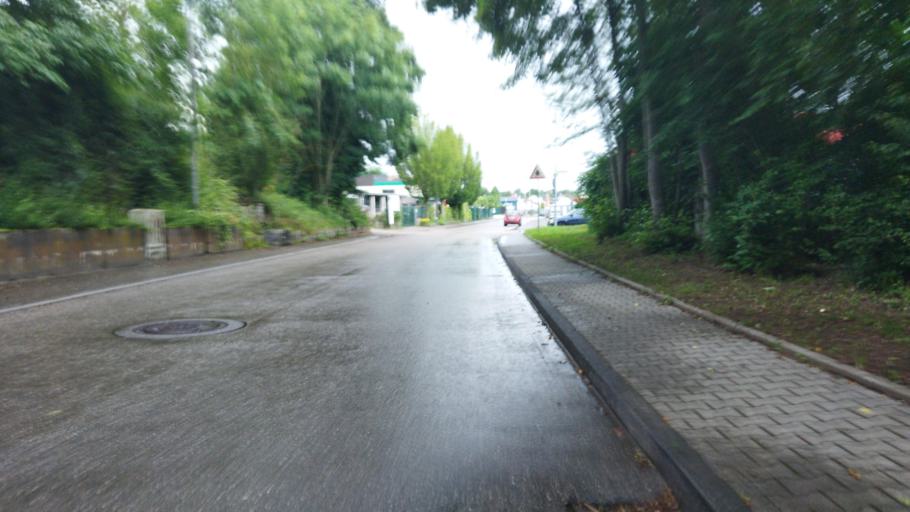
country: DE
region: Baden-Wuerttemberg
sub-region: Regierungsbezirk Stuttgart
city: Kirchardt
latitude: 49.2019
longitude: 9.0006
